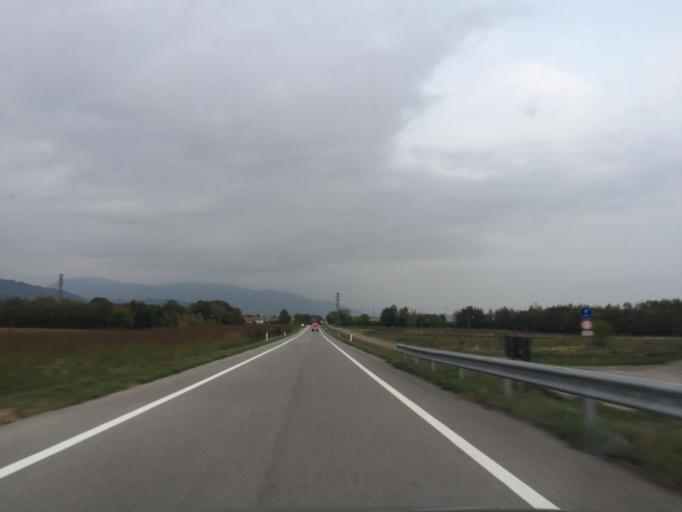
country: IT
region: Friuli Venezia Giulia
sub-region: Provincia di Pordenone
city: Vajont
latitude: 46.1552
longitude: 12.6944
